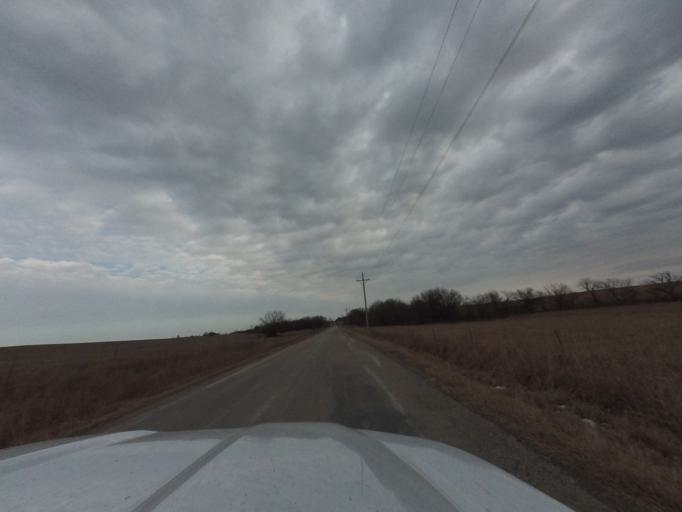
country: US
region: Kansas
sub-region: Chase County
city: Cottonwood Falls
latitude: 38.4311
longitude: -96.3732
